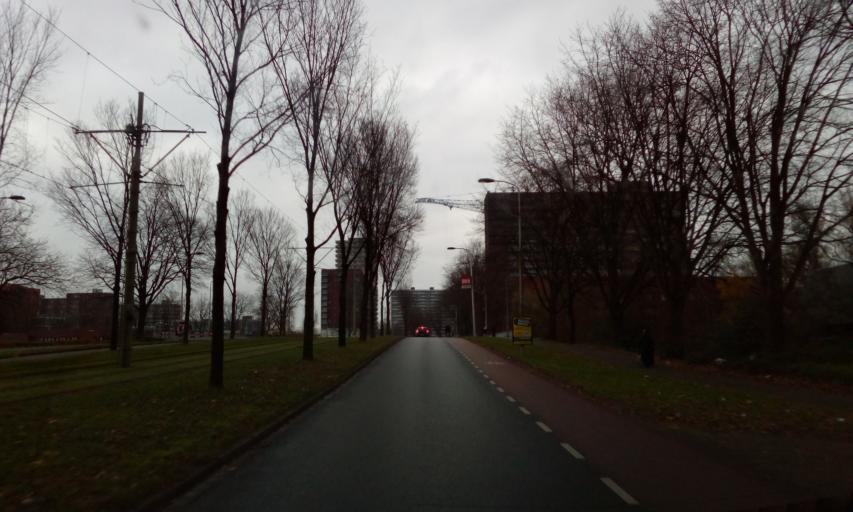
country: NL
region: South Holland
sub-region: Gemeente Delft
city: Delft
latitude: 51.9958
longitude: 4.3473
